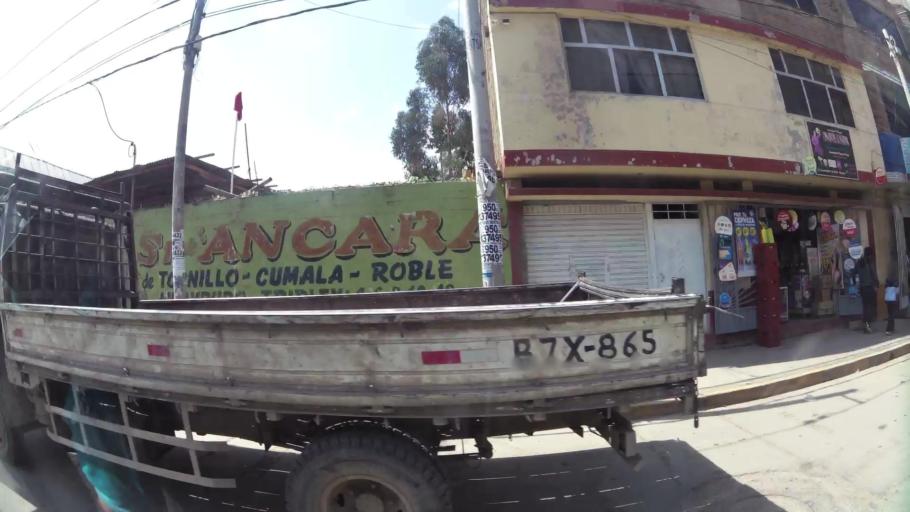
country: PE
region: Junin
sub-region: Provincia de Huancayo
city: El Tambo
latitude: -12.0848
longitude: -75.2083
